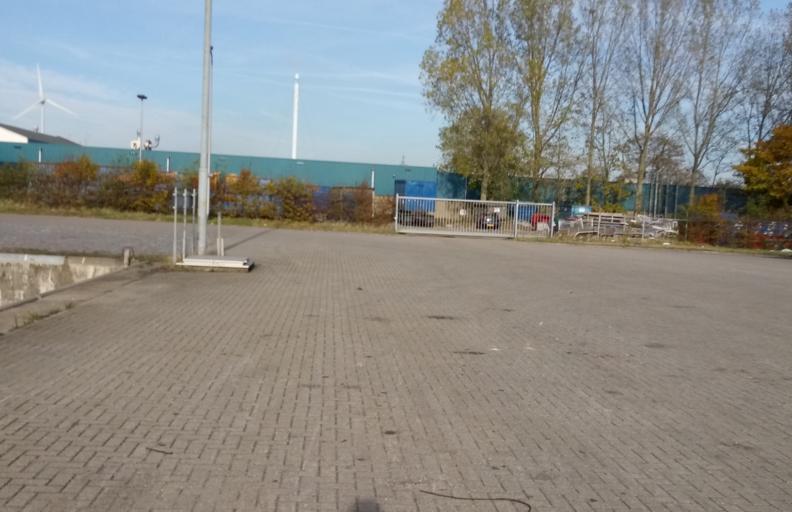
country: NL
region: Gelderland
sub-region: Gemeente Zutphen
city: Zutphen
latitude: 52.1563
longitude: 6.1951
